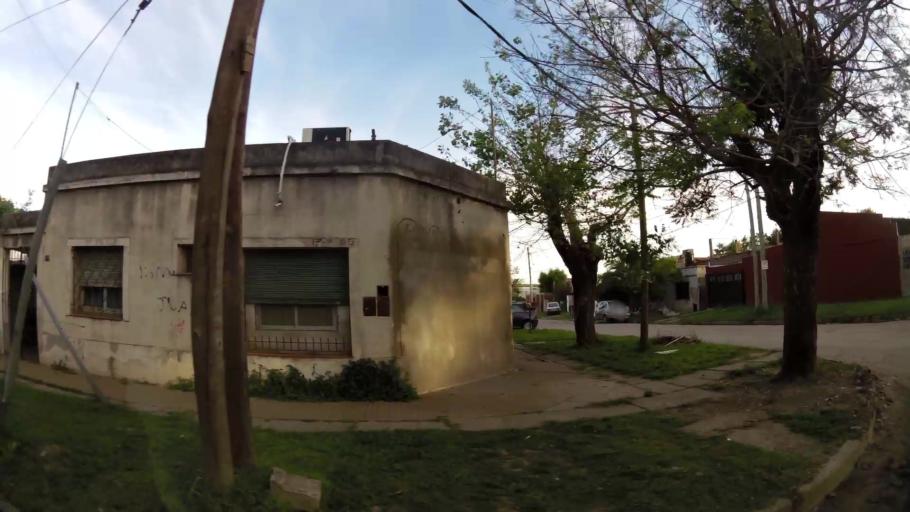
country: AR
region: Buenos Aires
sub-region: Partido de Almirante Brown
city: Adrogue
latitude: -34.7895
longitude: -58.3459
